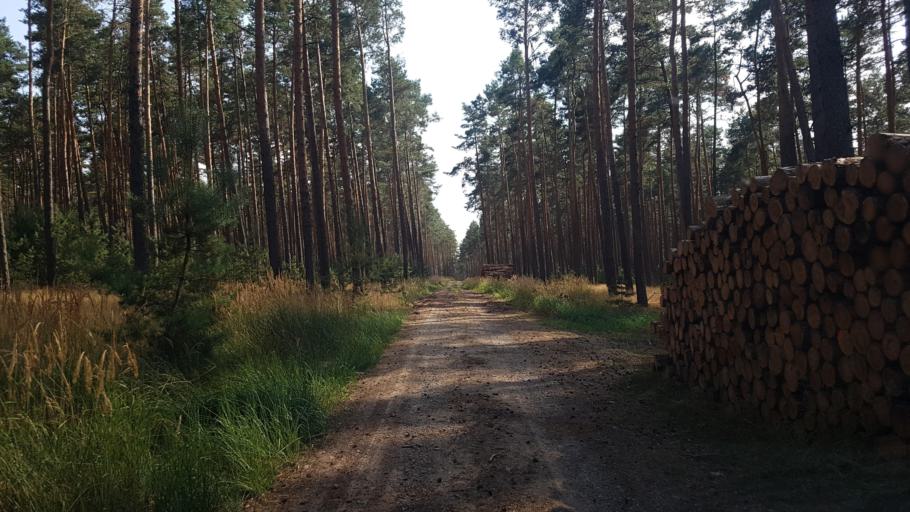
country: DE
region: Brandenburg
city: Dahme
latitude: 51.9664
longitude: 13.4188
